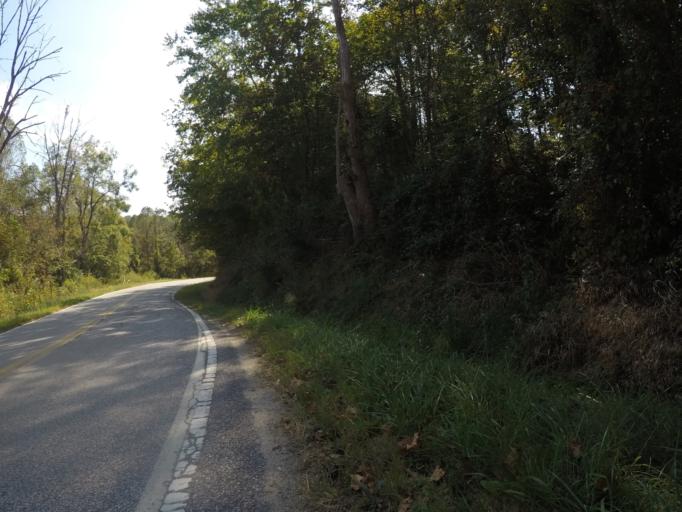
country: US
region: West Virginia
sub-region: Cabell County
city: Lesage
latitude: 38.5854
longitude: -82.4246
